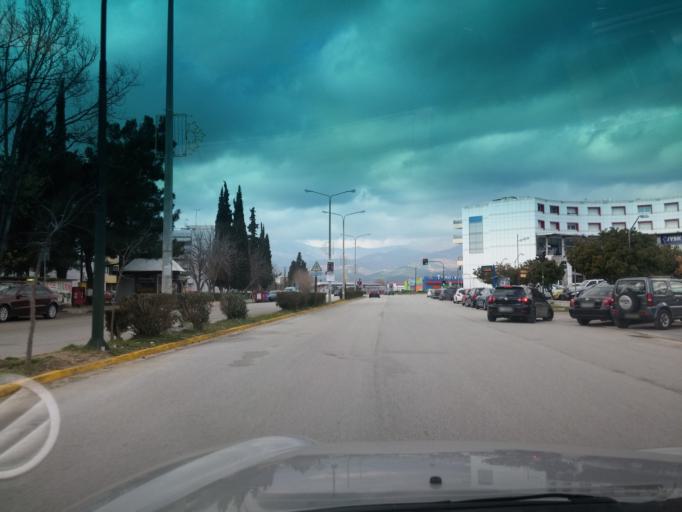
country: GR
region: East Macedonia and Thrace
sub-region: Nomos Rodopis
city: Komotini
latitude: 41.1246
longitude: 25.3941
